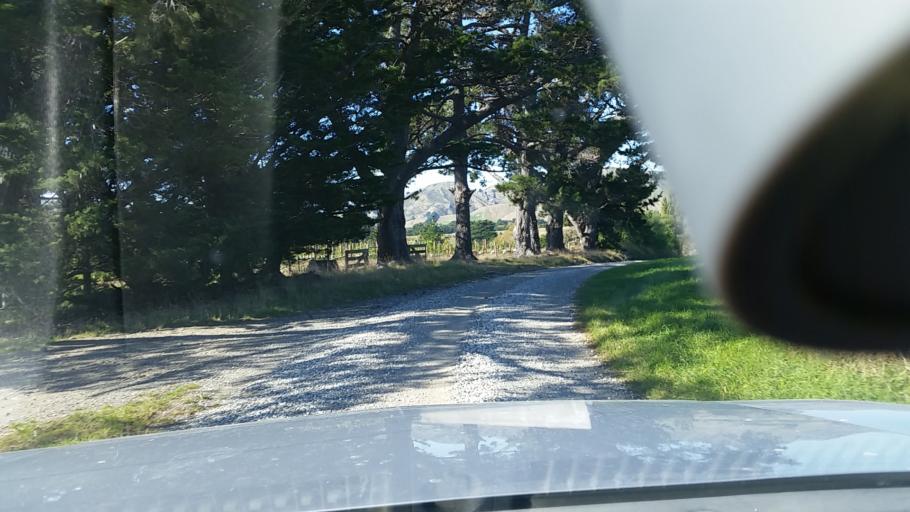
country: NZ
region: Marlborough
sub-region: Marlborough District
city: Blenheim
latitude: -41.8244
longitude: 174.1172
